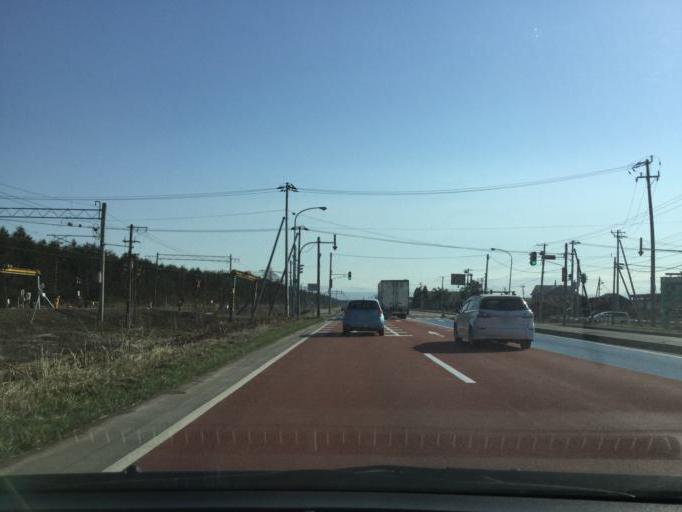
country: JP
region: Hokkaido
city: Iwamizawa
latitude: 43.1714
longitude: 141.6952
